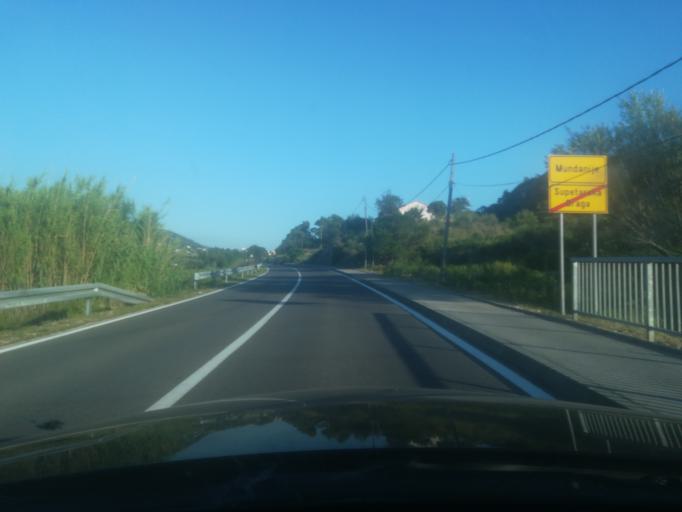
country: HR
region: Primorsko-Goranska
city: Supetarska Draga
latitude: 44.7819
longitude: 14.7484
